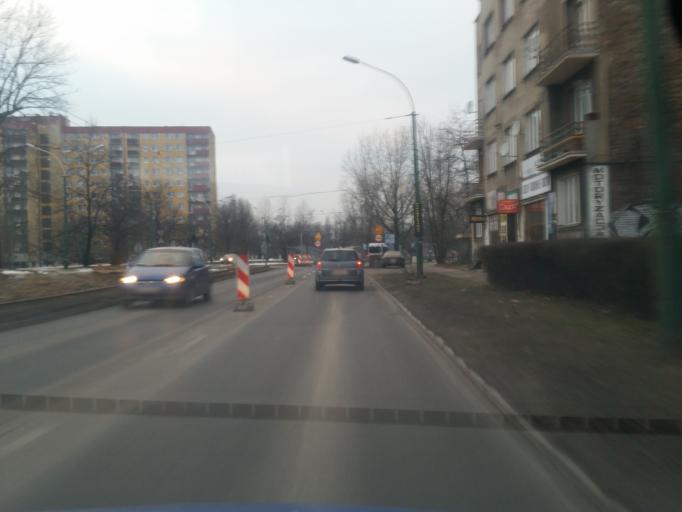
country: PL
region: Silesian Voivodeship
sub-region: Sosnowiec
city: Sosnowiec
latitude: 50.2803
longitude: 19.1100
